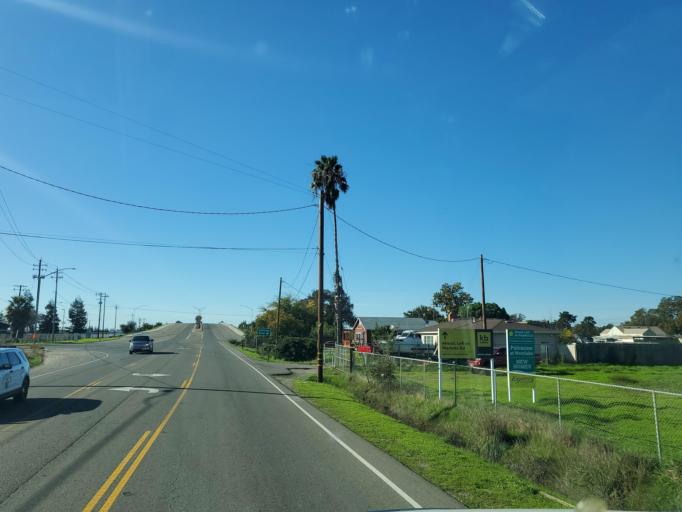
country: US
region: California
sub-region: San Joaquin County
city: Morada
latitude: 38.0574
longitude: -121.2716
